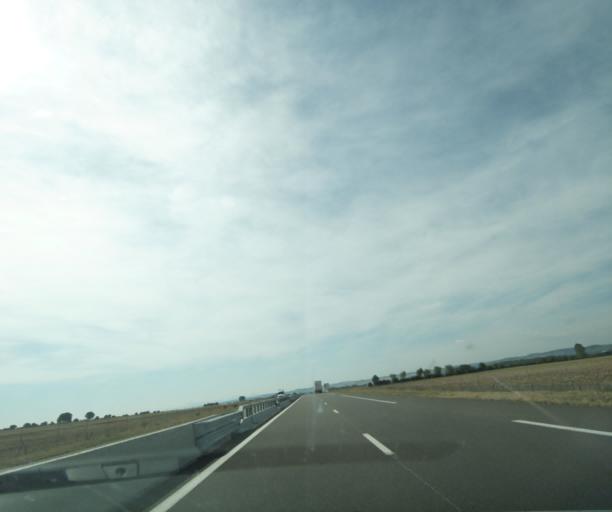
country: FR
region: Auvergne
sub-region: Departement de l'Allier
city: Gannat
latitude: 46.1116
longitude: 3.2686
